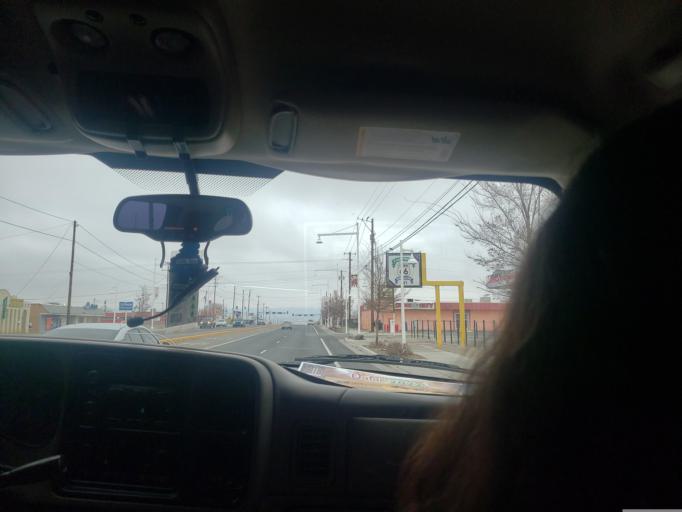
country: US
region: New Mexico
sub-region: Bernalillo County
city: Albuquerque
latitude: 35.0811
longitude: -106.7056
